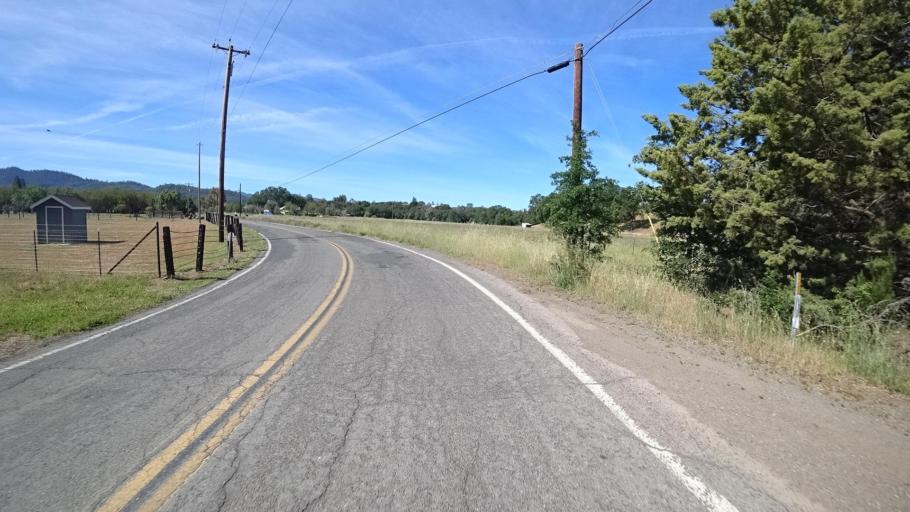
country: US
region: California
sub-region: Lake County
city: Kelseyville
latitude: 38.9619
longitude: -122.8383
